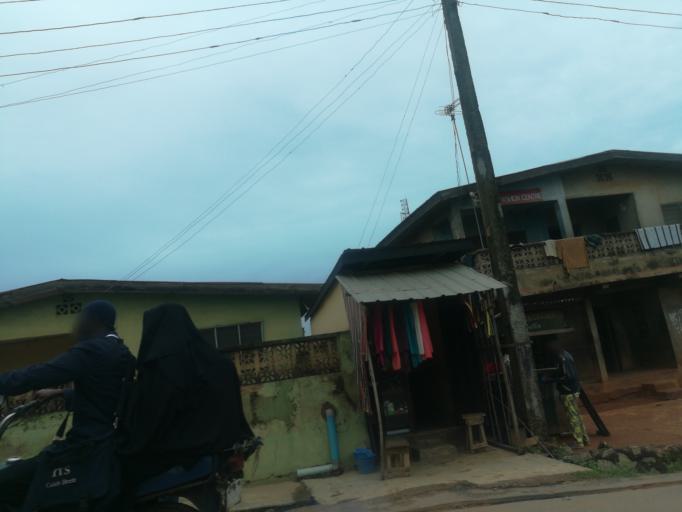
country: NG
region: Oyo
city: Ibadan
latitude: 7.3385
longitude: 3.9073
